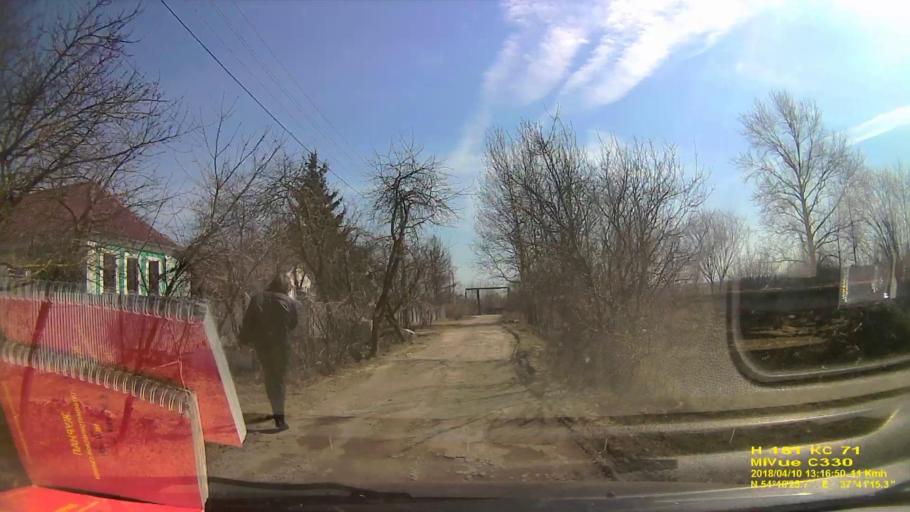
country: RU
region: Tula
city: Tula
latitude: 54.1738
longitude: 37.6876
